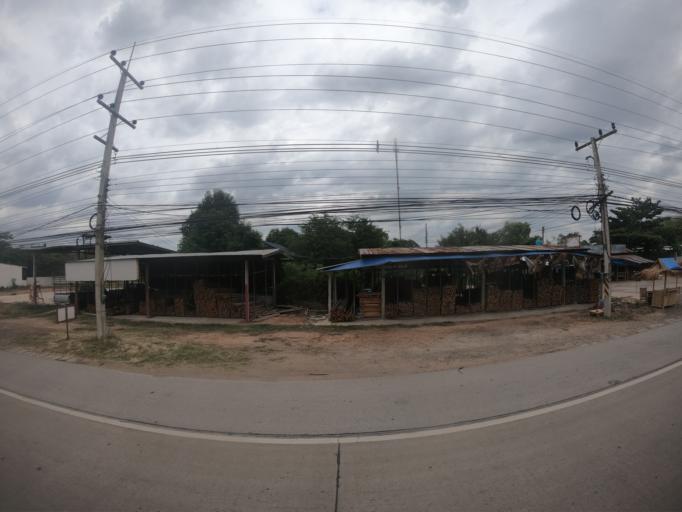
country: TH
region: Nakhon Ratchasima
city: Chok Chai
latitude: 14.7496
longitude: 102.1643
